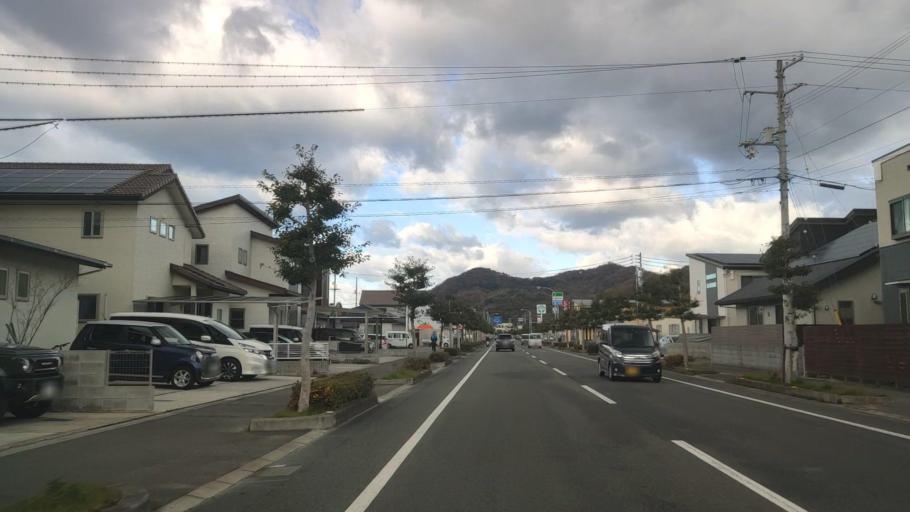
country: JP
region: Ehime
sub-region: Shikoku-chuo Shi
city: Matsuyama
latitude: 33.8689
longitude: 132.7236
